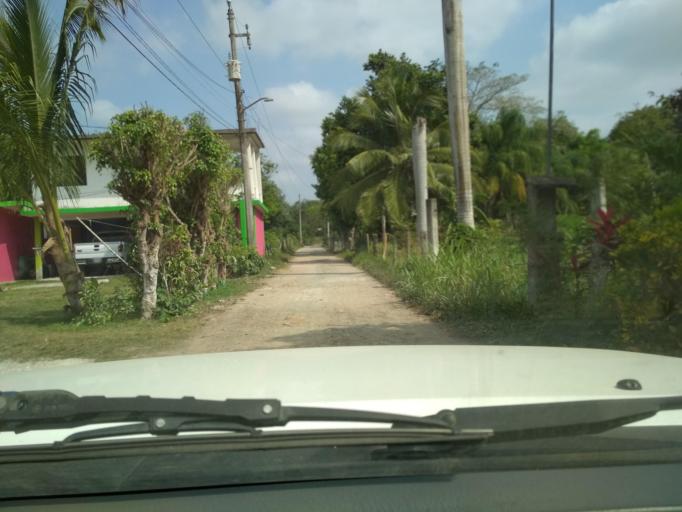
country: MX
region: Veracruz
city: El Tejar
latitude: 19.0776
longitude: -96.1700
